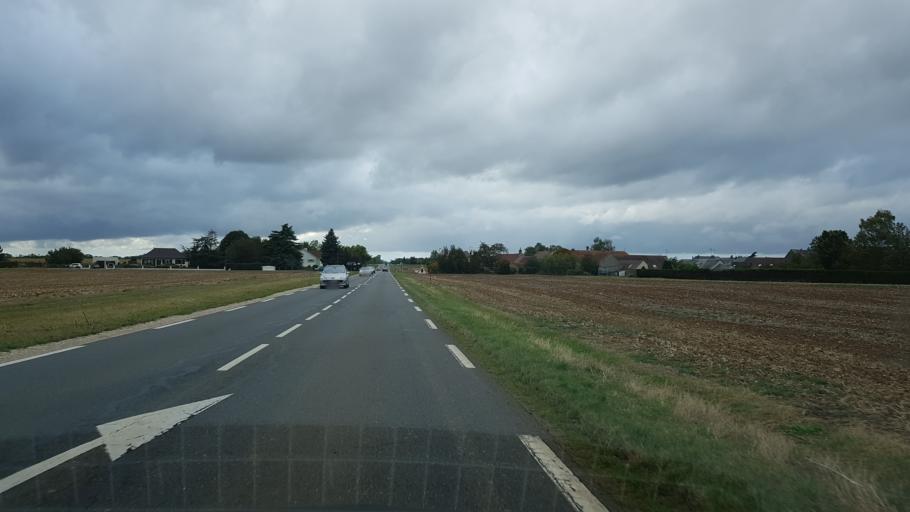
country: FR
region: Centre
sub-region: Departement du Loiret
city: Boynes
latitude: 48.1302
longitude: 2.3340
